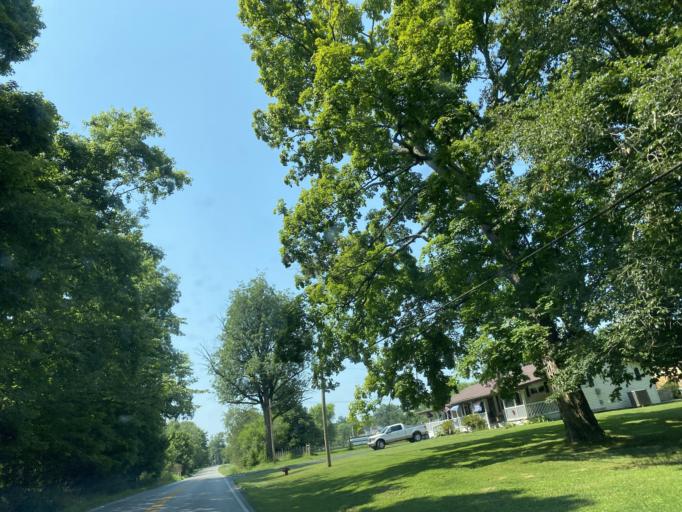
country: US
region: Kentucky
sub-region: Campbell County
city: Claryville
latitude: 38.8856
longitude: -84.4479
